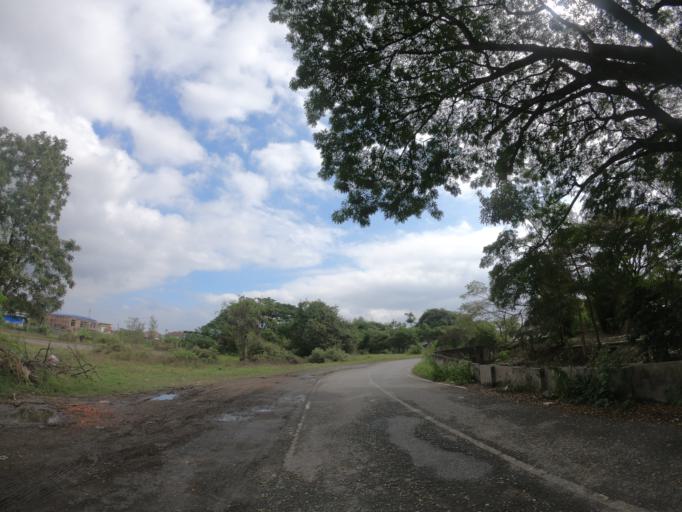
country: TH
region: Chiang Mai
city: Hang Dong
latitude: 18.7315
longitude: 98.9588
